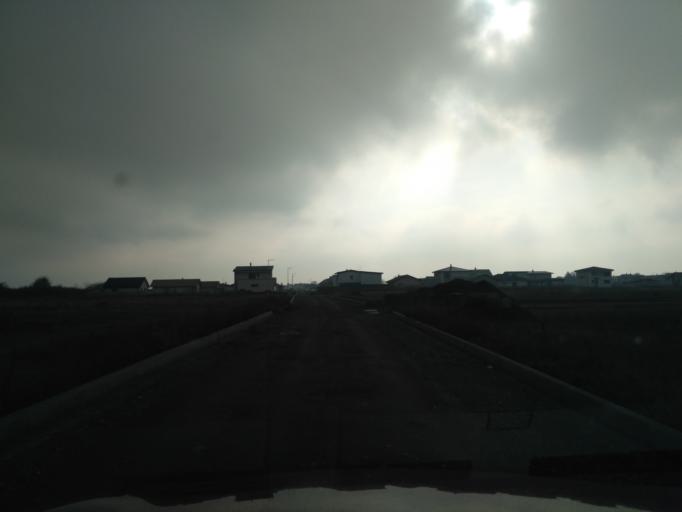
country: SK
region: Kosicky
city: Kosice
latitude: 48.6756
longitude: 21.3255
